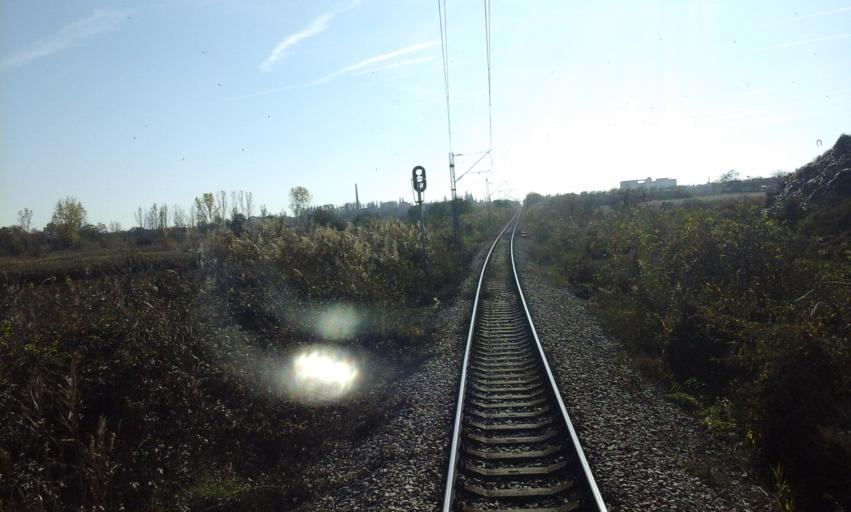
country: RS
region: Autonomna Pokrajina Vojvodina
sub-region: Severnobacki Okrug
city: Subotica
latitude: 46.0806
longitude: 19.6900
